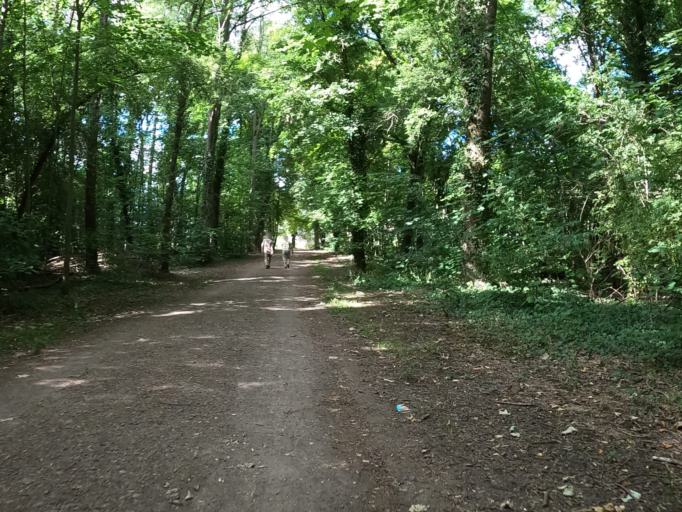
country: DE
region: Hesse
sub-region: Regierungsbezirk Darmstadt
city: Gross-Gerau
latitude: 49.9085
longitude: 8.4818
